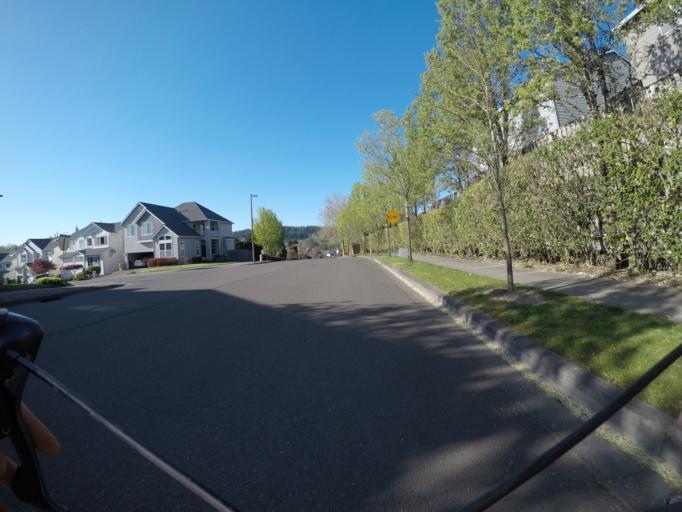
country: US
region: Oregon
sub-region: Washington County
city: King City
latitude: 45.4207
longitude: -122.8450
